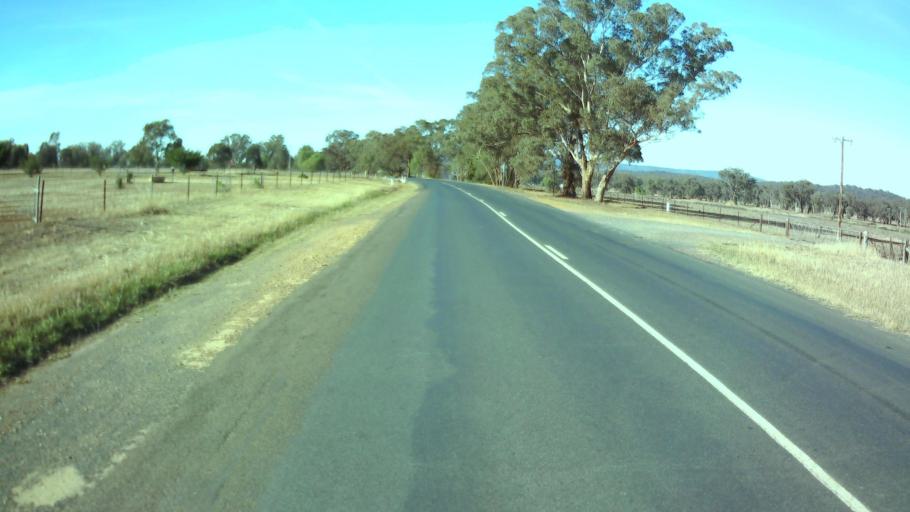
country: AU
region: New South Wales
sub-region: Weddin
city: Grenfell
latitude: -33.9066
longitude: 148.1470
